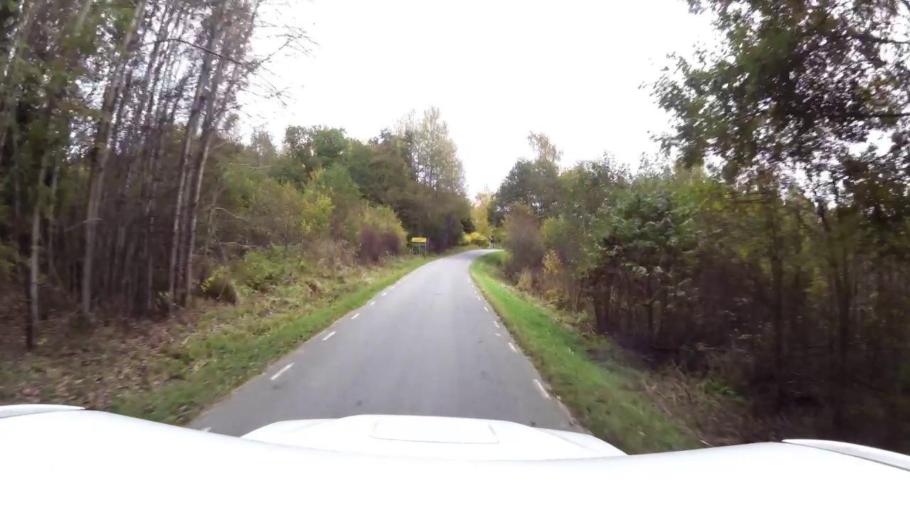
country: SE
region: OEstergoetland
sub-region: Linkopings Kommun
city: Ljungsbro
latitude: 58.5251
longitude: 15.4735
